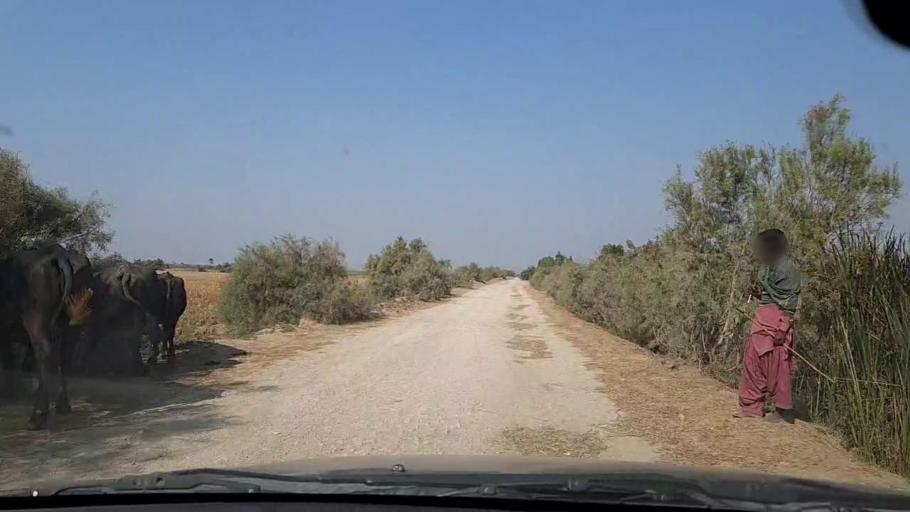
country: PK
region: Sindh
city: Mirpur Sakro
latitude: 24.3487
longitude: 67.6831
